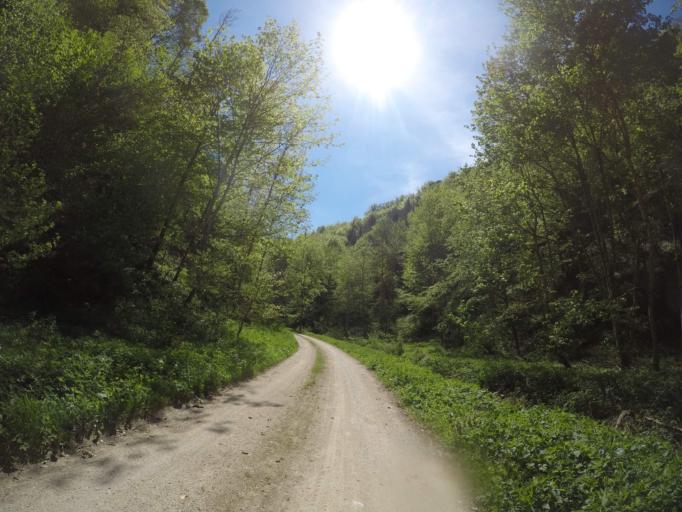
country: DE
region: Baden-Wuerttemberg
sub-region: Tuebingen Region
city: Schelklingen
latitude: 48.4050
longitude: 9.7293
